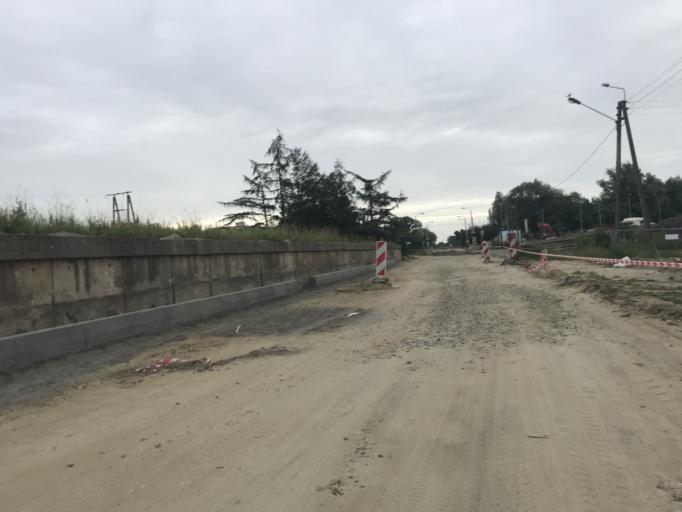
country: PL
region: Pomeranian Voivodeship
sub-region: Gdansk
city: Gdansk
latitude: 54.3412
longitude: 18.6851
